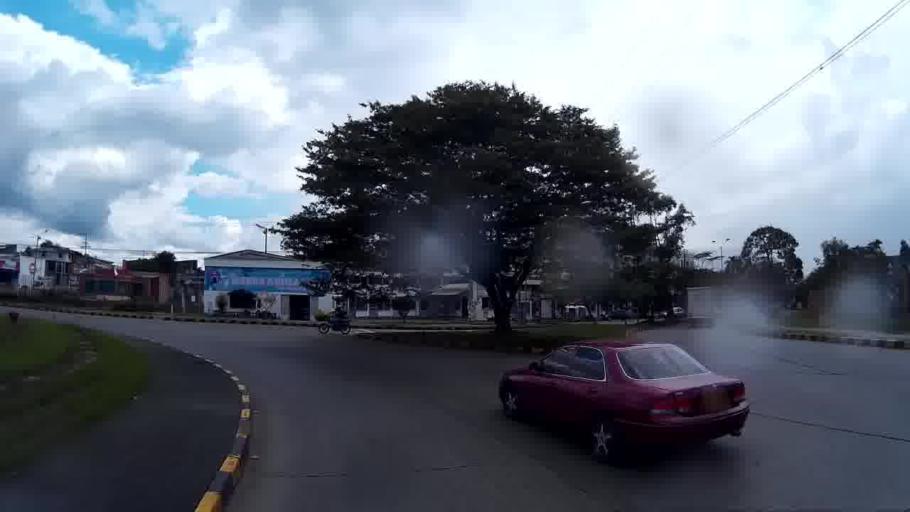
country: CO
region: Quindio
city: Armenia
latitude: 4.5442
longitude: -75.6658
